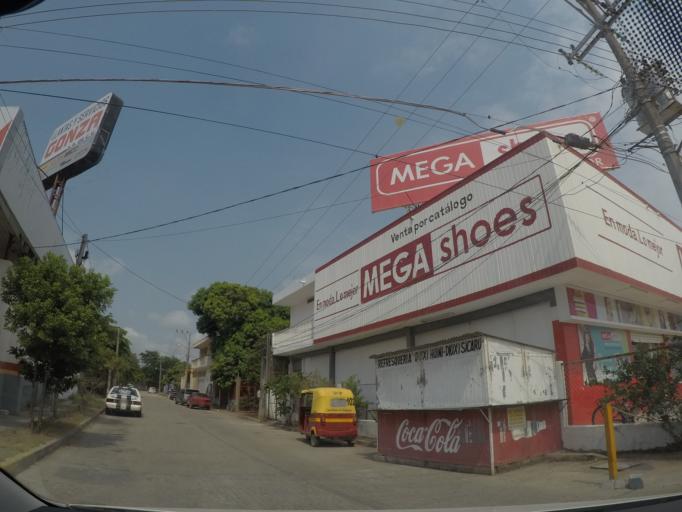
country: MX
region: Oaxaca
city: Juchitan de Zaragoza
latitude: 16.4471
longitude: -95.0256
